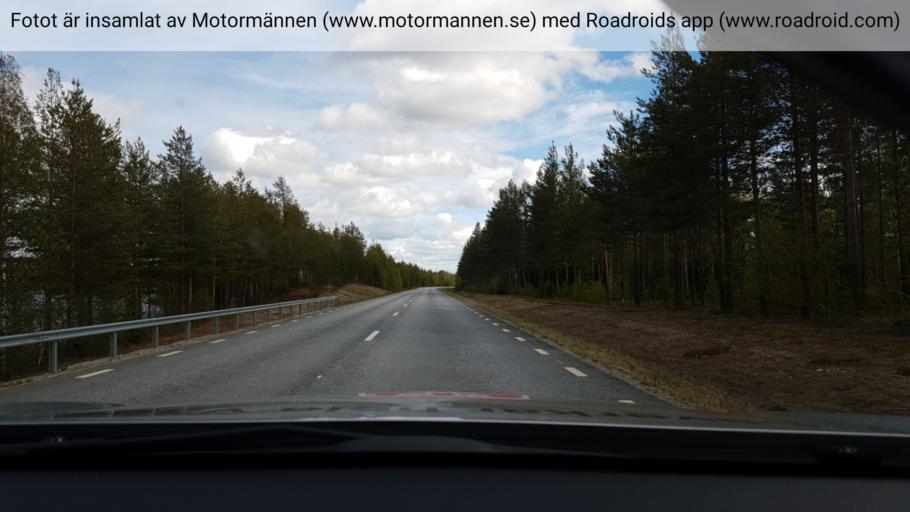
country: SE
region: Vaesterbotten
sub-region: Asele Kommun
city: Insjon
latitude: 64.1952
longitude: 17.7672
